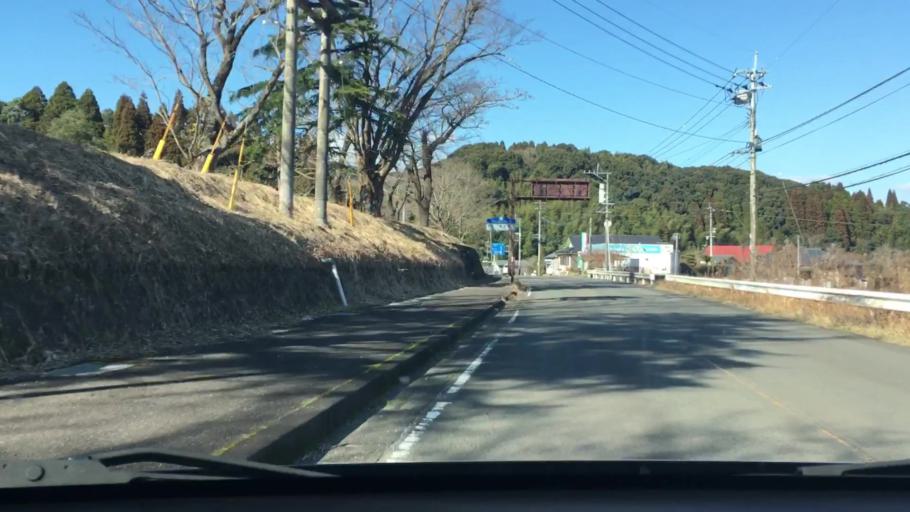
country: JP
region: Kagoshima
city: Satsumasendai
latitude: 31.7771
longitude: 130.4006
